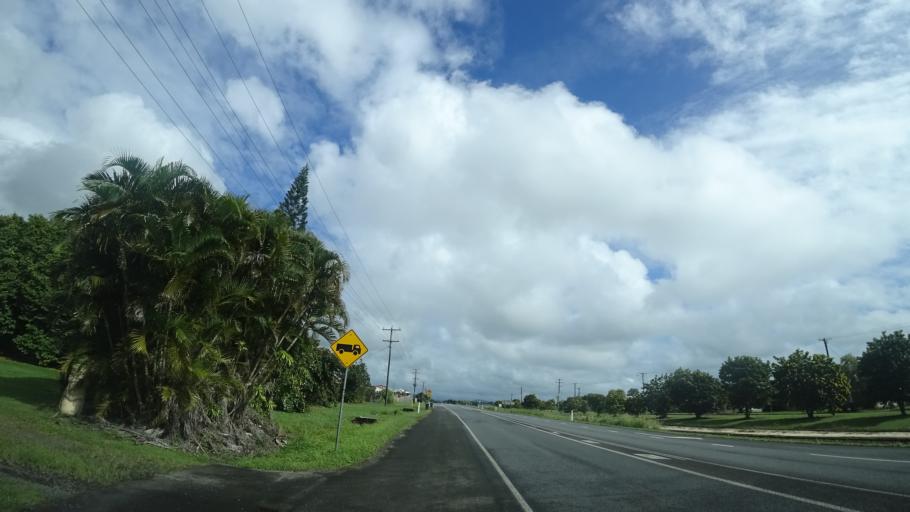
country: AU
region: Queensland
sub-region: Cassowary Coast
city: Innisfail
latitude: -17.5915
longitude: 146.0637
